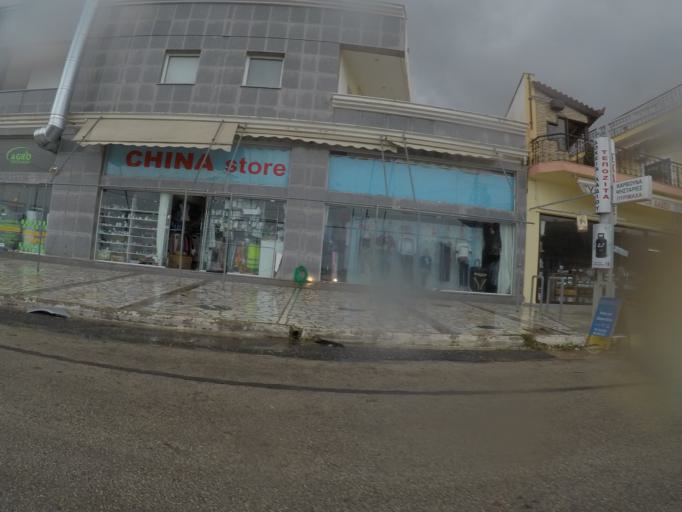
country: GR
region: Peloponnese
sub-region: Nomos Messinias
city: Kyparissia
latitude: 37.2520
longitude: 21.6733
